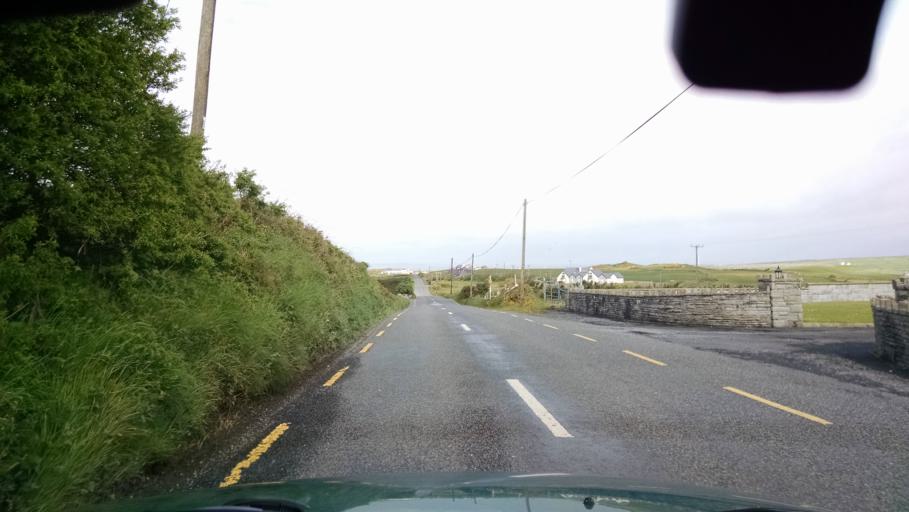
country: IE
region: Connaught
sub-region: County Galway
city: Bearna
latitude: 53.0099
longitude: -9.3617
